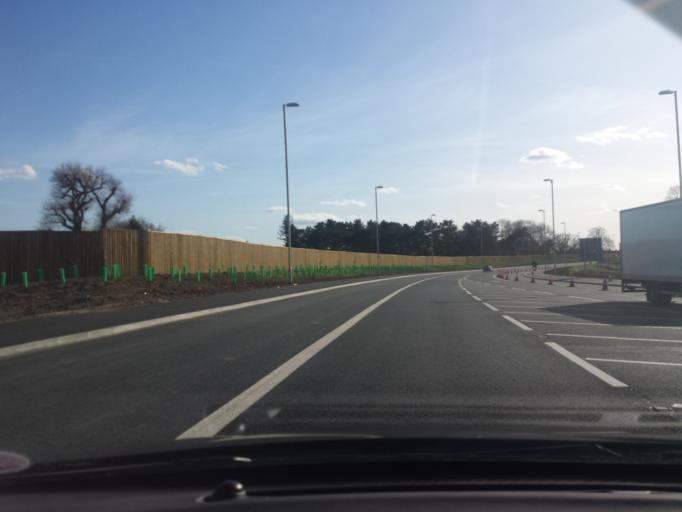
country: GB
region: England
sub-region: Essex
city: Colchester
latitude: 51.9178
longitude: 0.9018
